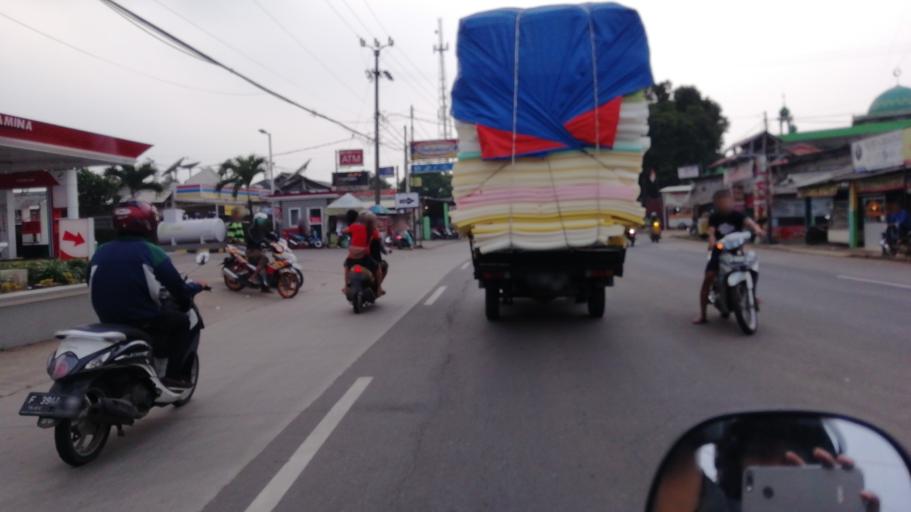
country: ID
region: West Java
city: Parung
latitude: -6.4802
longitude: 106.7315
